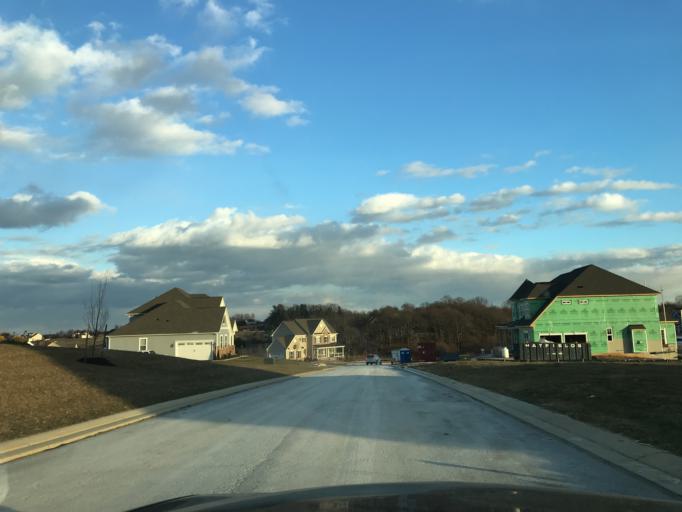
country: US
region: Maryland
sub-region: Harford County
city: Bel Air North
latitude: 39.5945
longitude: -76.3810
